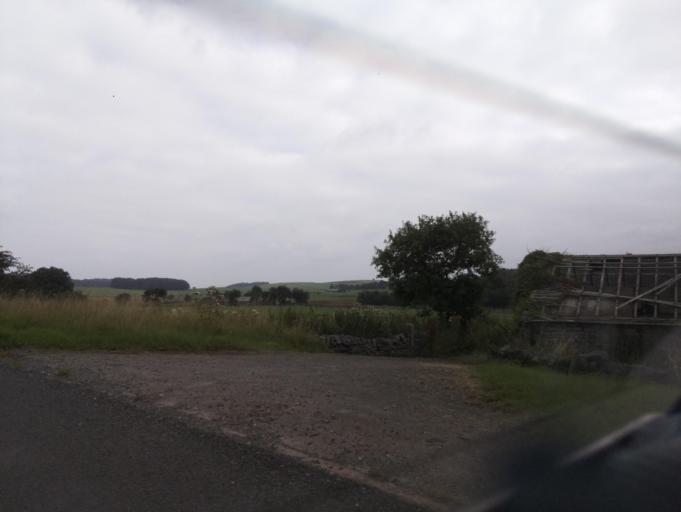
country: GB
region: England
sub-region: Staffordshire
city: Mayfield
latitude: 53.0272
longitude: -1.8737
